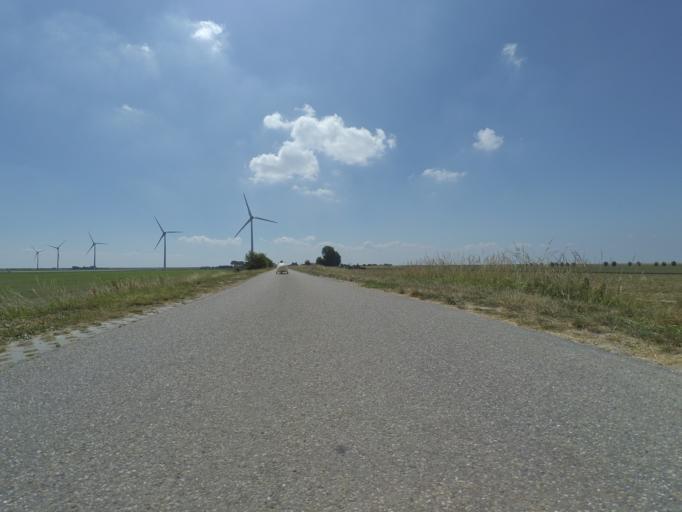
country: NL
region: Zeeland
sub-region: Gemeente Reimerswaal
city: Yerseke
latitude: 51.5712
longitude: 4.0407
